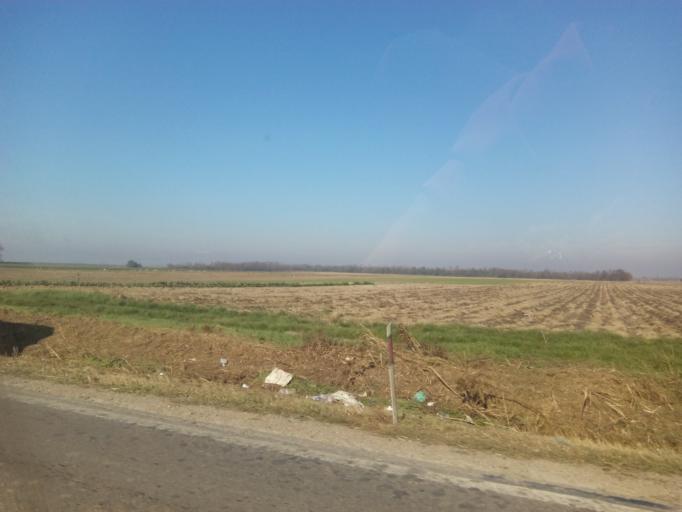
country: RS
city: Glozan
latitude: 45.2418
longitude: 19.6118
